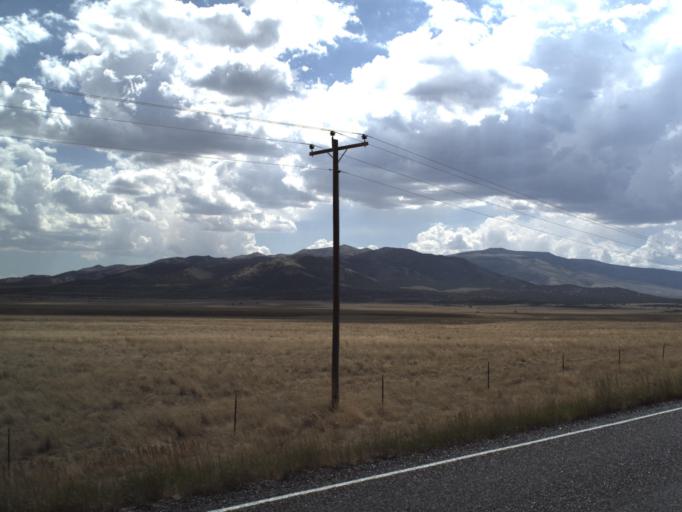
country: US
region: Idaho
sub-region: Power County
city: American Falls
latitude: 41.9697
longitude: -113.1165
